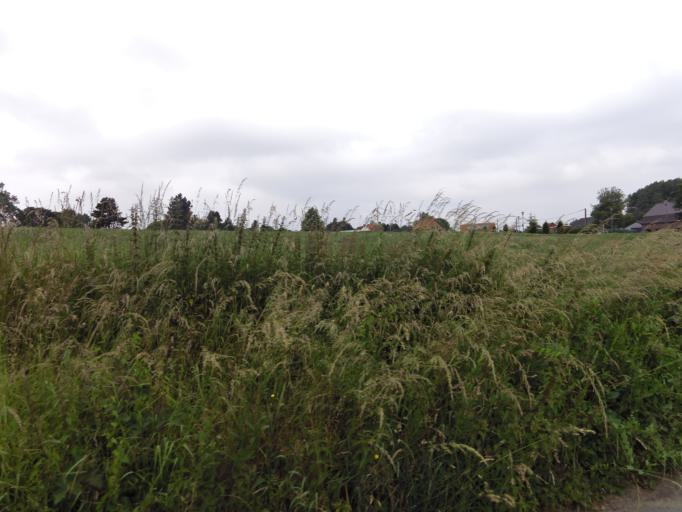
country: FR
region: Nord-Pas-de-Calais
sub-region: Departement du Nord
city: Saint-Jans-Cappel
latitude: 50.7870
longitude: 2.7699
